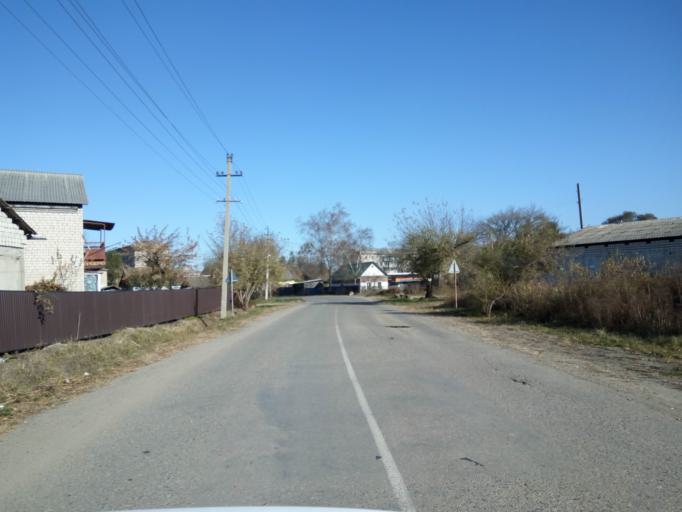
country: RU
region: Primorskiy
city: Dal'nerechensk
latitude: 45.9346
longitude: 133.7182
